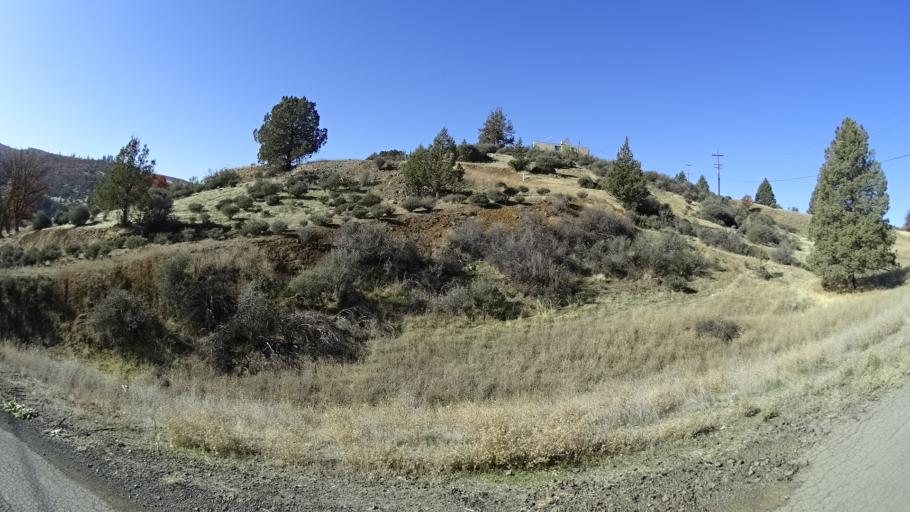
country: US
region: California
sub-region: Siskiyou County
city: Montague
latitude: 41.8990
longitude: -122.5228
